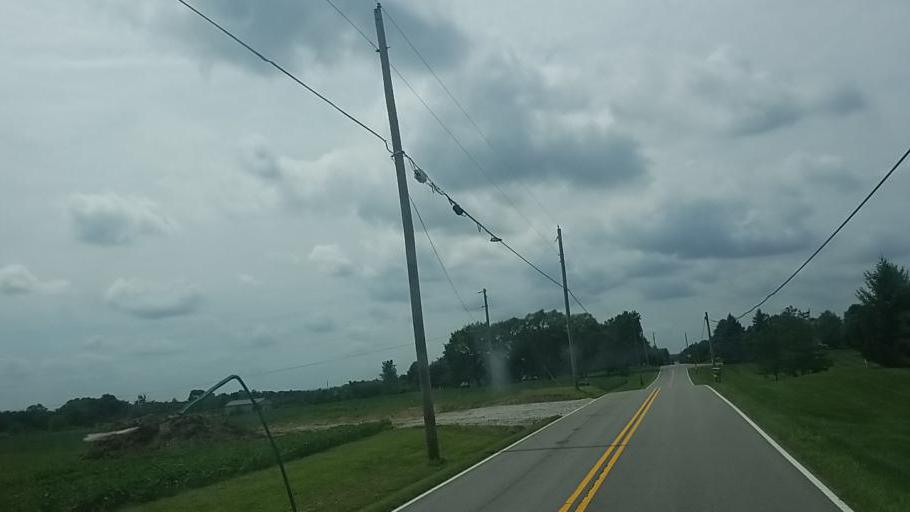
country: US
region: Ohio
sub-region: Fairfield County
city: Lithopolis
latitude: 39.7507
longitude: -82.8135
